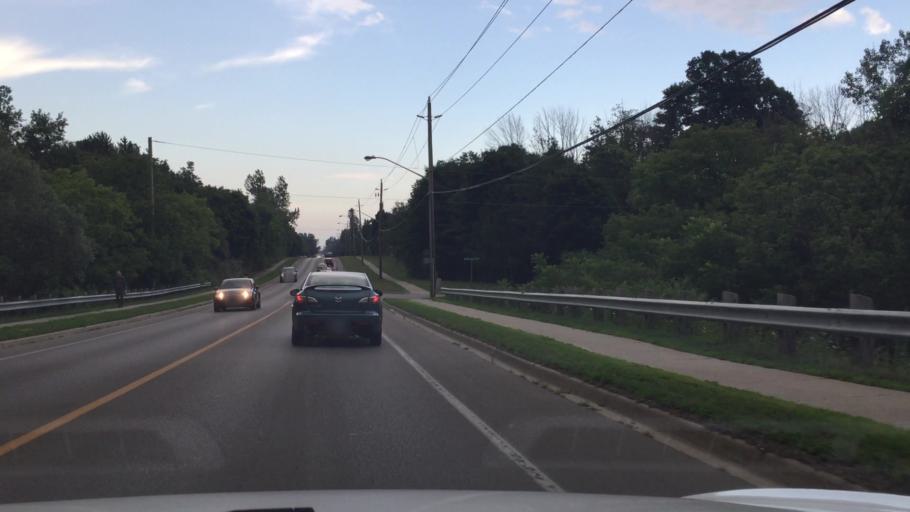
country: CA
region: Ontario
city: Oshawa
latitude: 43.9117
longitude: -78.8004
